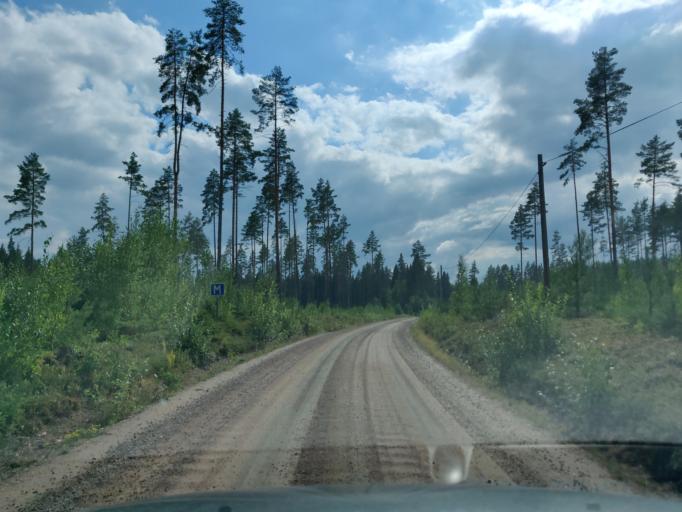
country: SE
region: Vaermland
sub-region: Hagfors Kommun
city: Hagfors
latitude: 59.9892
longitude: 13.5646
